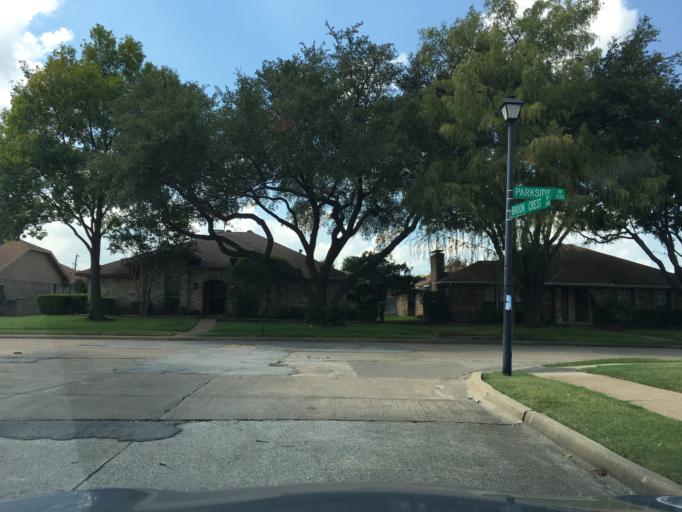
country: US
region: Texas
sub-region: Dallas County
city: Garland
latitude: 32.9417
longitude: -96.6394
